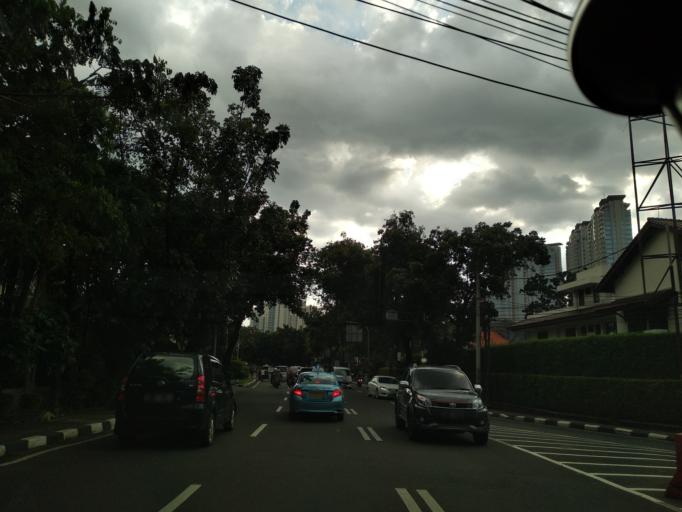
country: ID
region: Jakarta Raya
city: Jakarta
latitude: -6.2334
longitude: 106.7941
